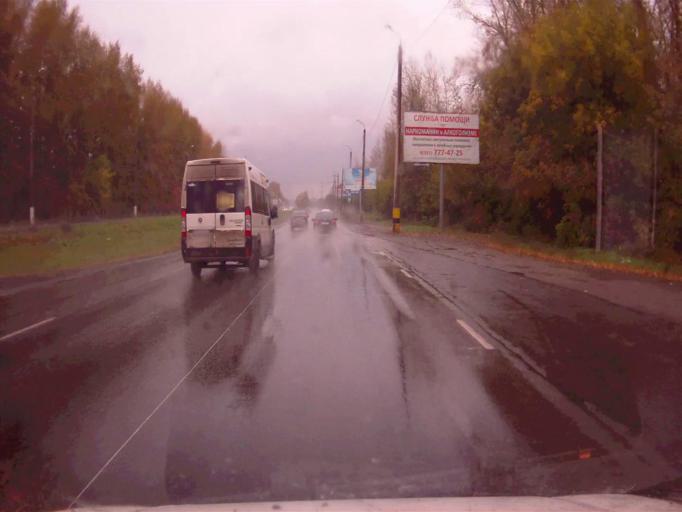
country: RU
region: Chelyabinsk
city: Dolgoderevenskoye
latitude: 55.2436
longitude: 61.3603
